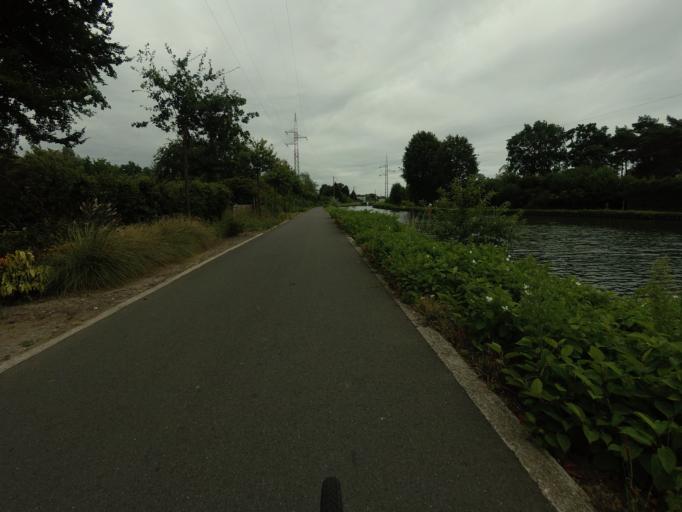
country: BE
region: Flanders
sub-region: Provincie Antwerpen
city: Brasschaat
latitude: 51.2924
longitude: 4.5462
